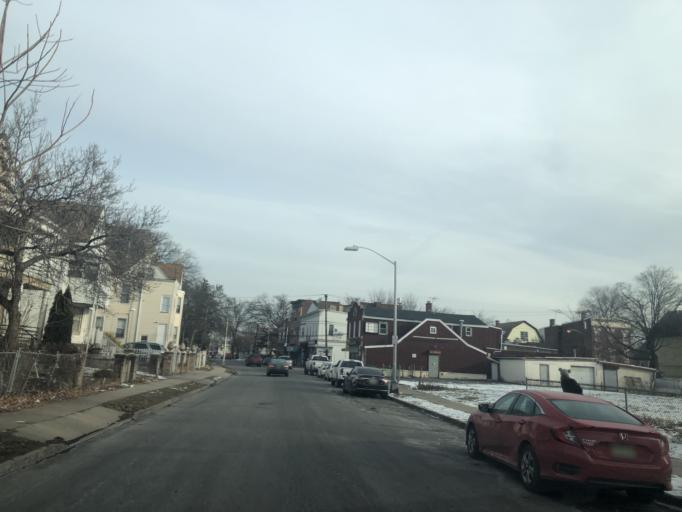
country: US
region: New Jersey
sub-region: Essex County
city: Orange
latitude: 40.7664
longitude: -74.2314
